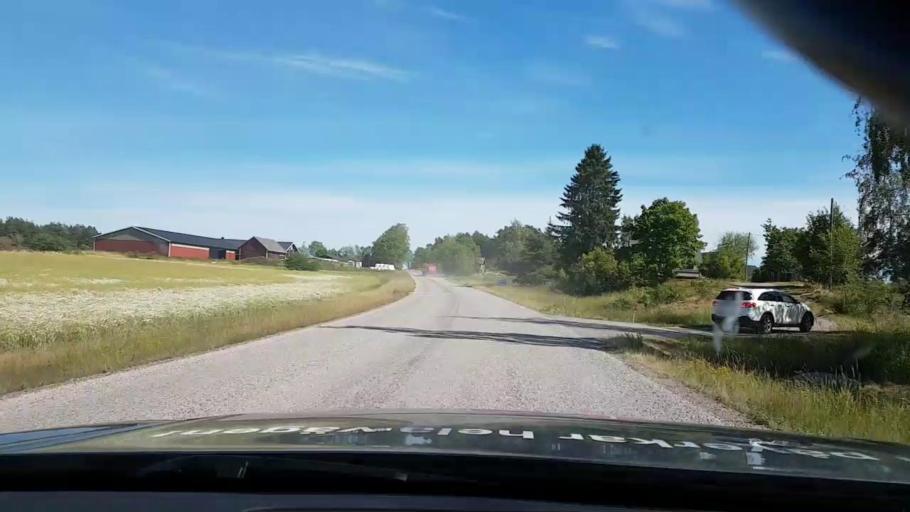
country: SE
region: Kalmar
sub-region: Vasterviks Kommun
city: Forserum
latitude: 57.9402
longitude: 16.4549
